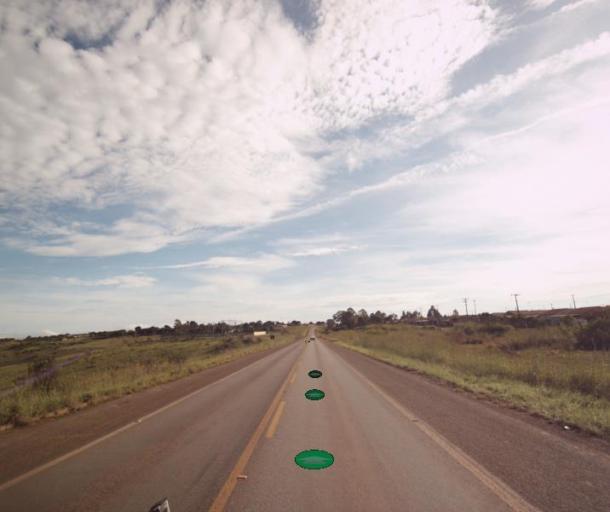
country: BR
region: Federal District
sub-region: Brasilia
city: Brasilia
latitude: -15.7458
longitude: -48.4110
